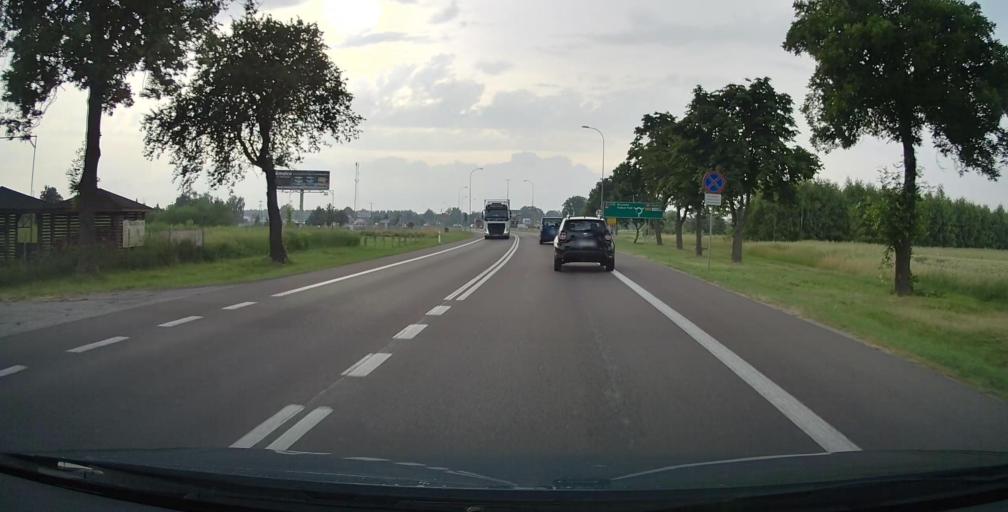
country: PL
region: Masovian Voivodeship
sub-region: Siedlce
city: Siedlce
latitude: 52.1311
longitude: 22.3319
